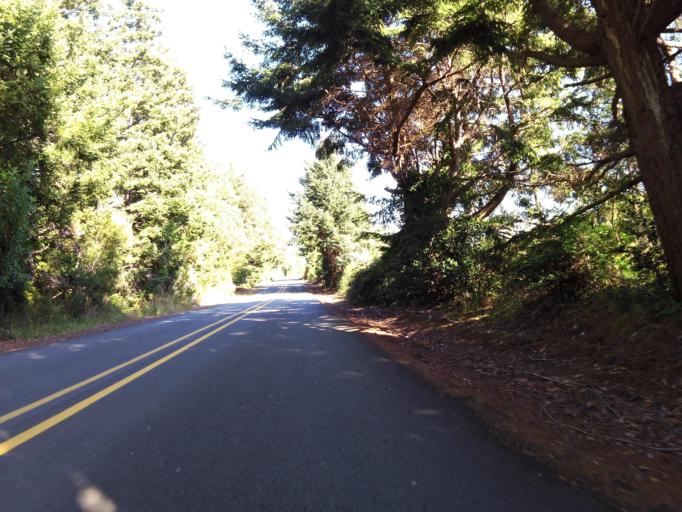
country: US
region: Oregon
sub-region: Coos County
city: Bandon
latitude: 43.0397
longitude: -124.4115
